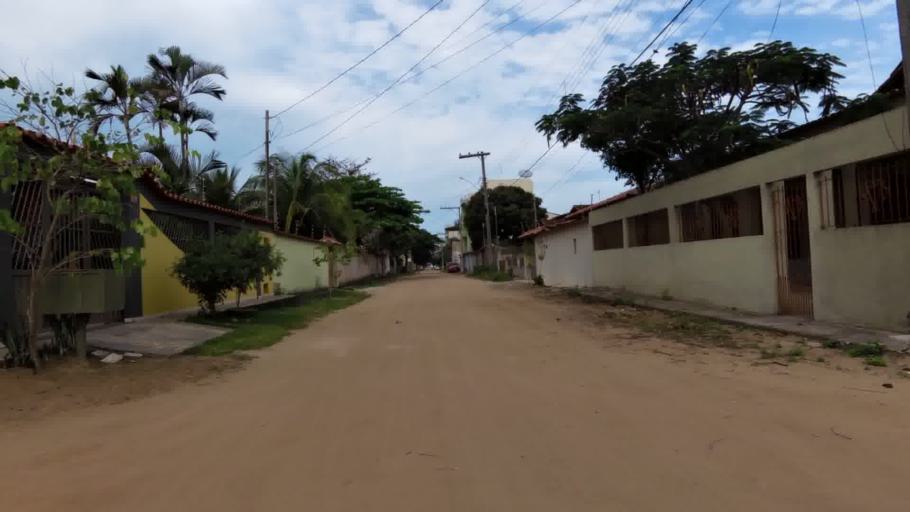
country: BR
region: Espirito Santo
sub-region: Piuma
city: Piuma
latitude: -20.8413
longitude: -40.7350
